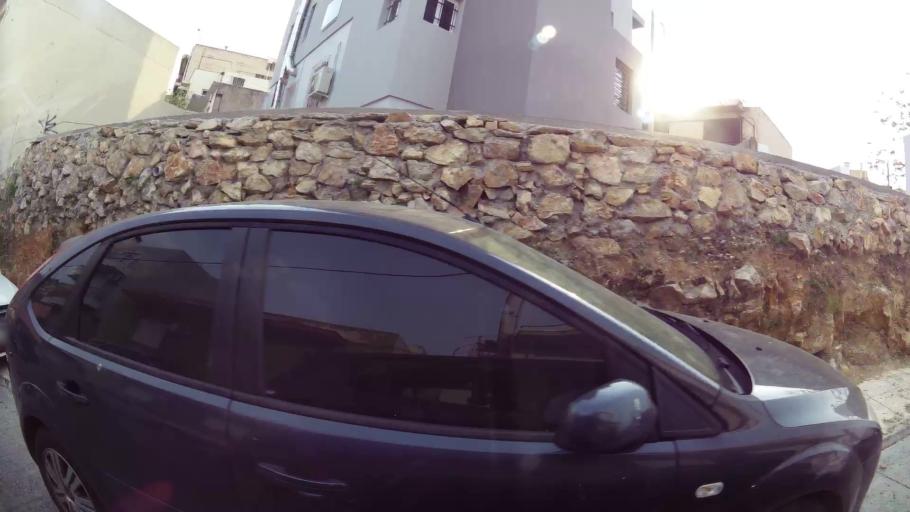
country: GR
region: Attica
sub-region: Nomarchia Athinas
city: Kipseli
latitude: 37.9974
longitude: 23.7553
